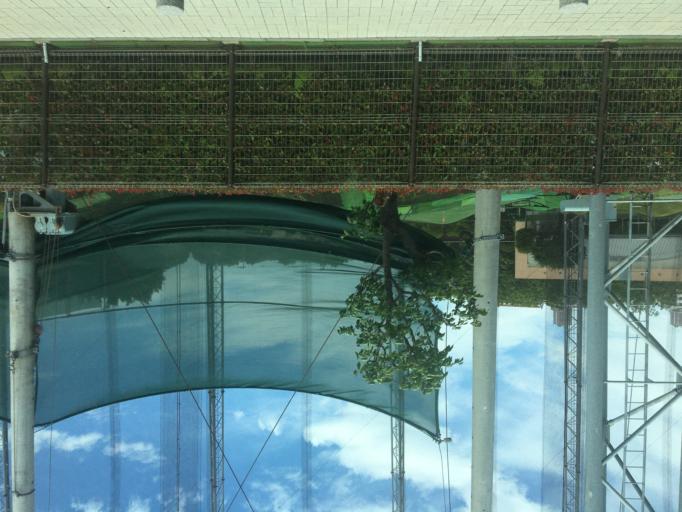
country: JP
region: Tokyo
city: Higashimurayama-shi
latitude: 35.7517
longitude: 139.4768
